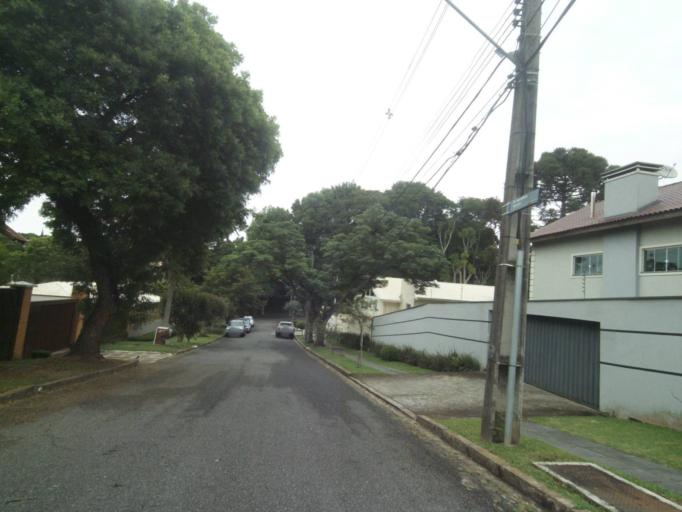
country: BR
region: Parana
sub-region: Curitiba
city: Curitiba
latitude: -25.4071
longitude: -49.2873
